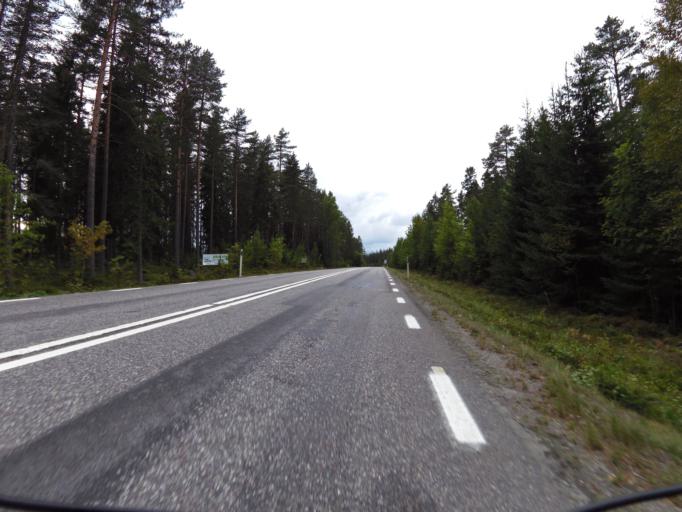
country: SE
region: Gaevleborg
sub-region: Ockelbo Kommun
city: Ockelbo
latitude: 60.8841
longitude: 16.8122
